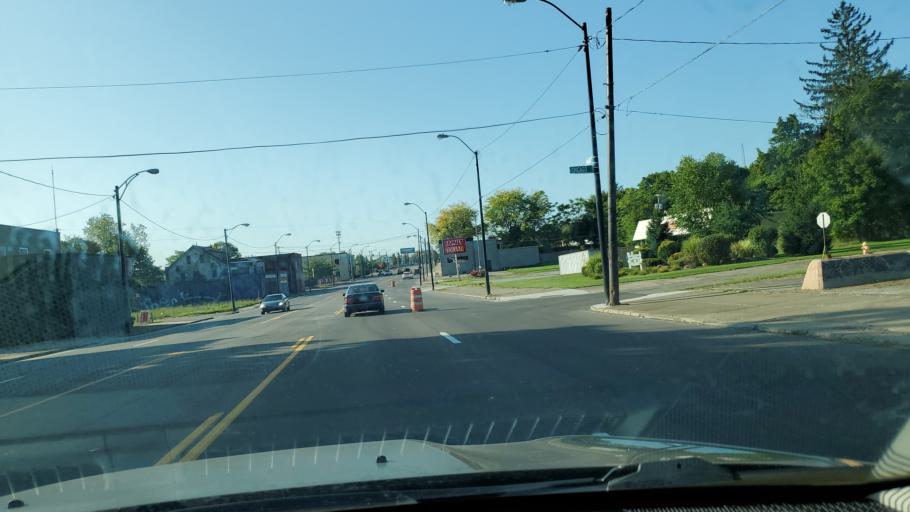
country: US
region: Ohio
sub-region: Mahoning County
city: Youngstown
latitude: 41.0783
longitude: -80.6570
